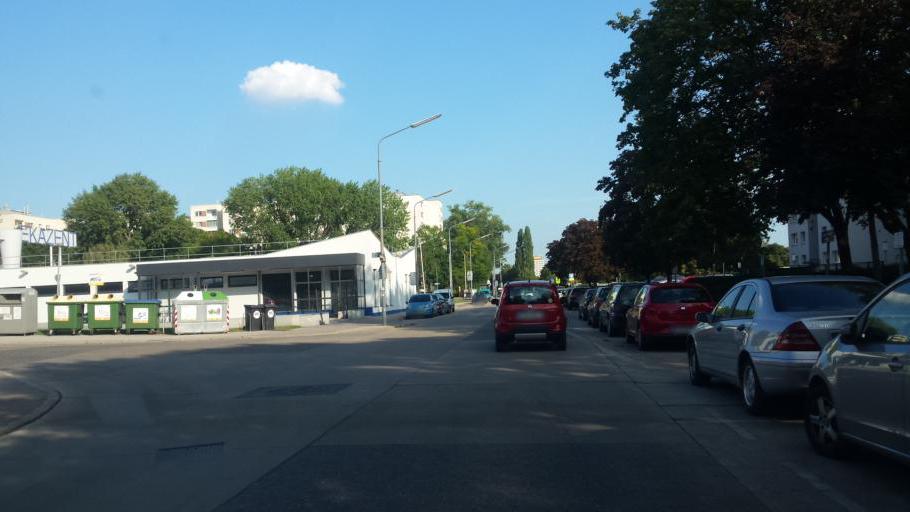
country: AT
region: Lower Austria
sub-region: Politischer Bezirk Wien-Umgebung
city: Leopoldsdorf
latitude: 48.1459
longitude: 16.3904
